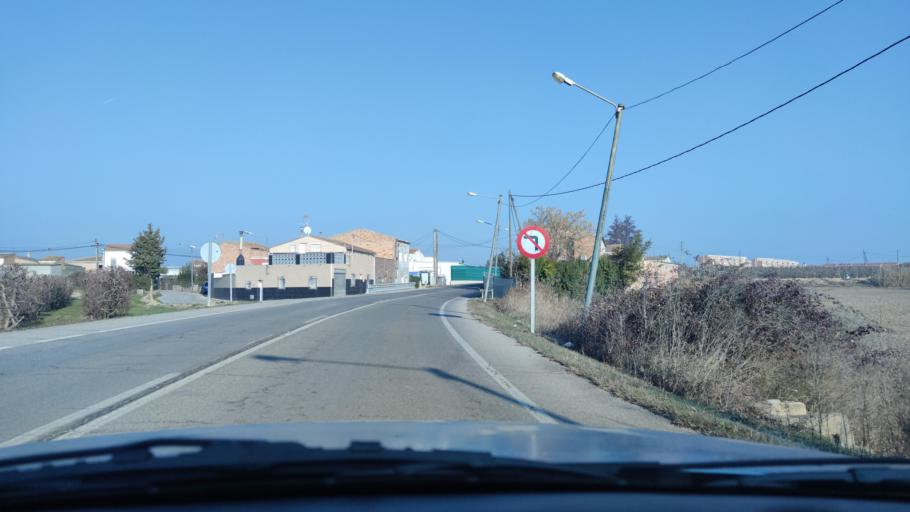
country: ES
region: Catalonia
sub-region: Provincia de Lleida
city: Lleida
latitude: 41.6426
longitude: 0.6354
